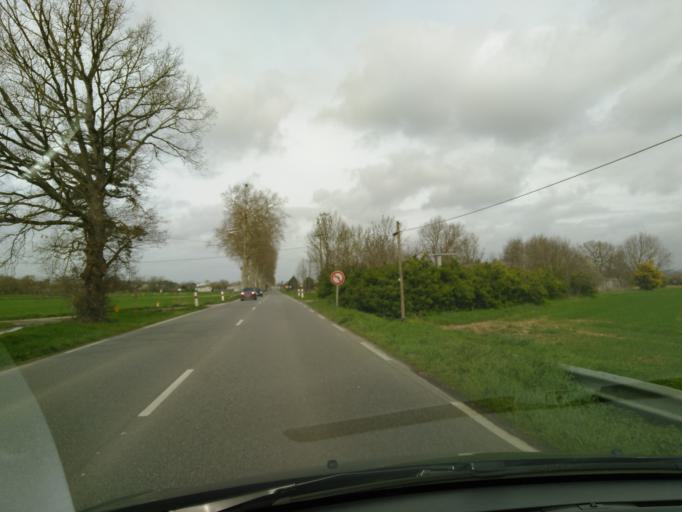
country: FR
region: Midi-Pyrenees
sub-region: Departement de la Haute-Garonne
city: Merville
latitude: 43.7489
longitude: 1.3059
